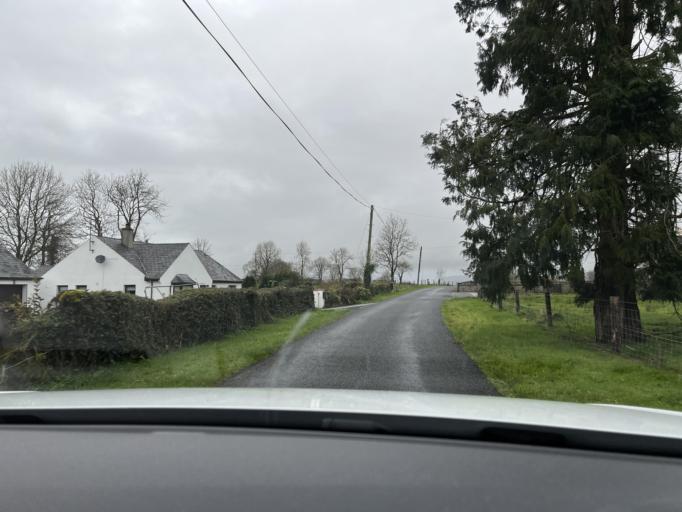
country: IE
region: Connaught
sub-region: County Leitrim
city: Manorhamilton
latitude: 54.2942
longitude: -8.1378
